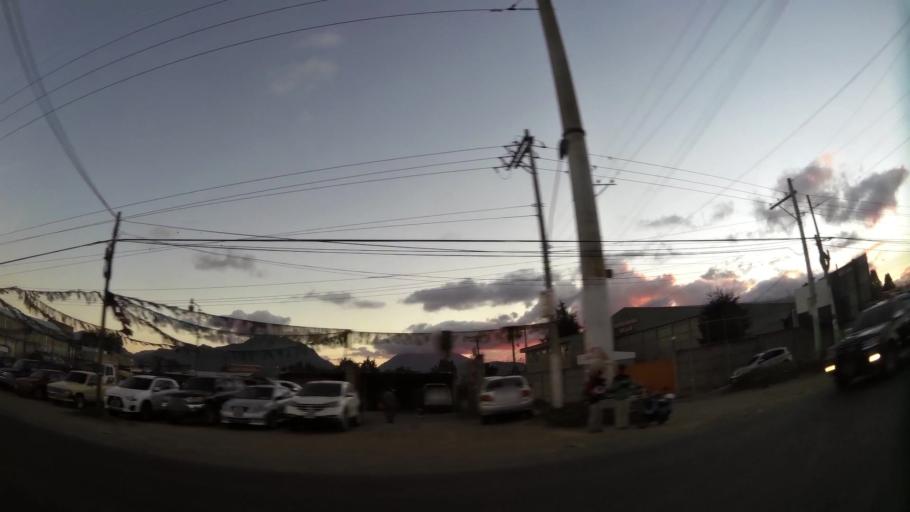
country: GT
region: Quetzaltenango
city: Olintepeque
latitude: 14.8616
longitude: -91.5268
